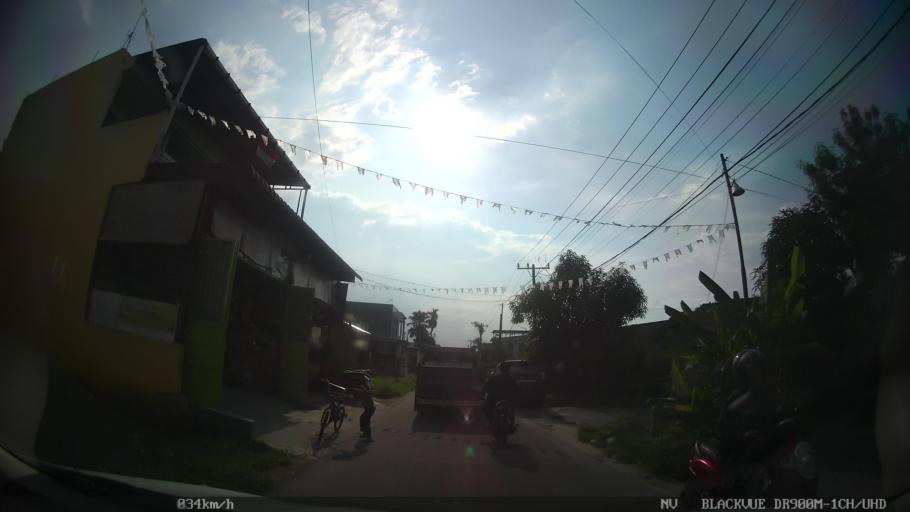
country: ID
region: North Sumatra
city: Percut
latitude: 3.5940
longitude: 98.7699
